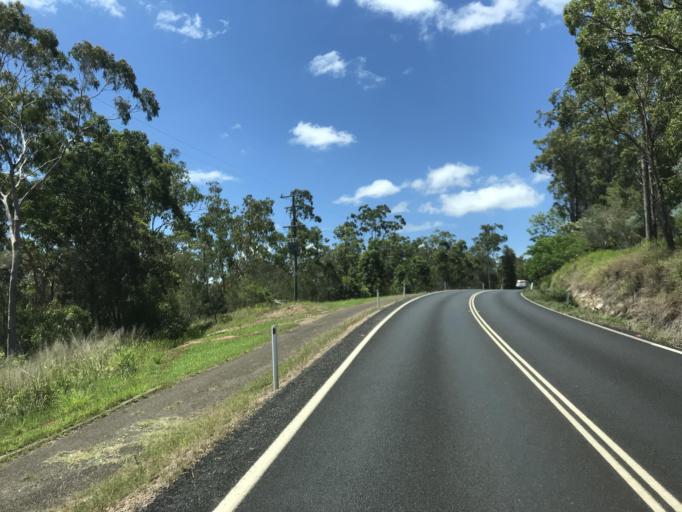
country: AU
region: Queensland
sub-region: Tablelands
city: Atherton
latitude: -17.3937
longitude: 145.3878
